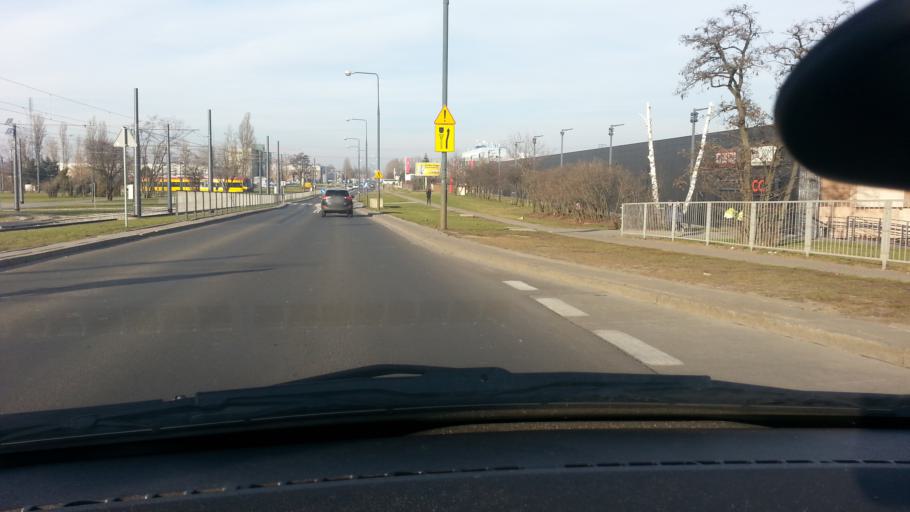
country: PL
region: Masovian Voivodeship
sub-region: Warszawa
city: Targowek
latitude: 52.2980
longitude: 21.0240
